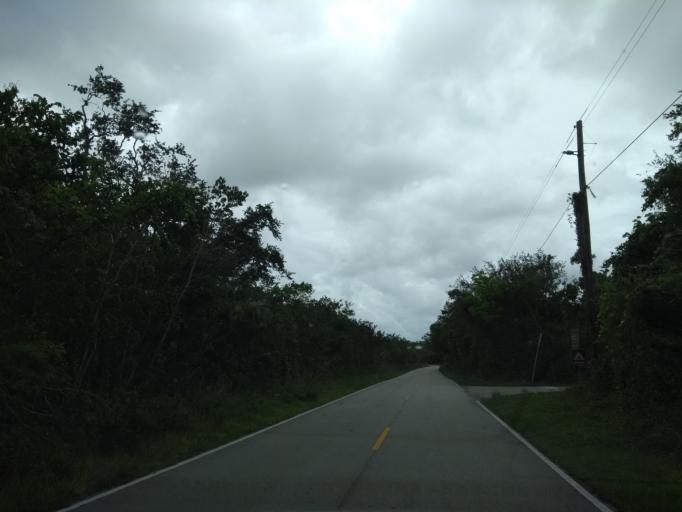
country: US
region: Florida
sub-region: Miami-Dade County
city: The Hammocks
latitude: 25.7612
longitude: -80.9191
